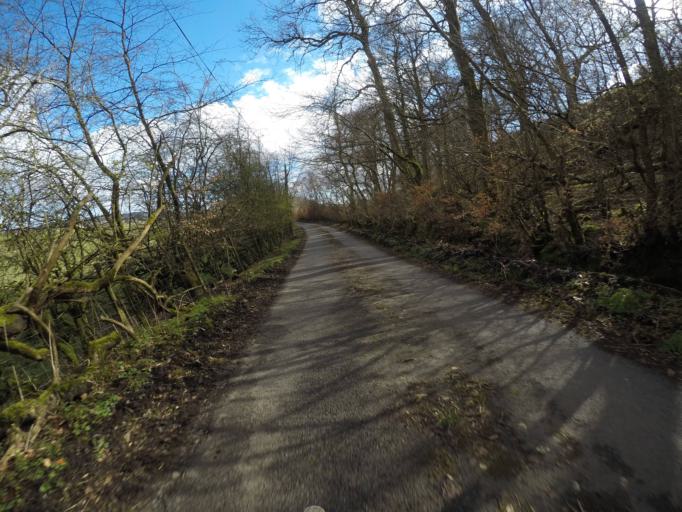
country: GB
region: Scotland
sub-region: North Ayrshire
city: Beith
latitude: 55.7156
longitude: -4.6360
